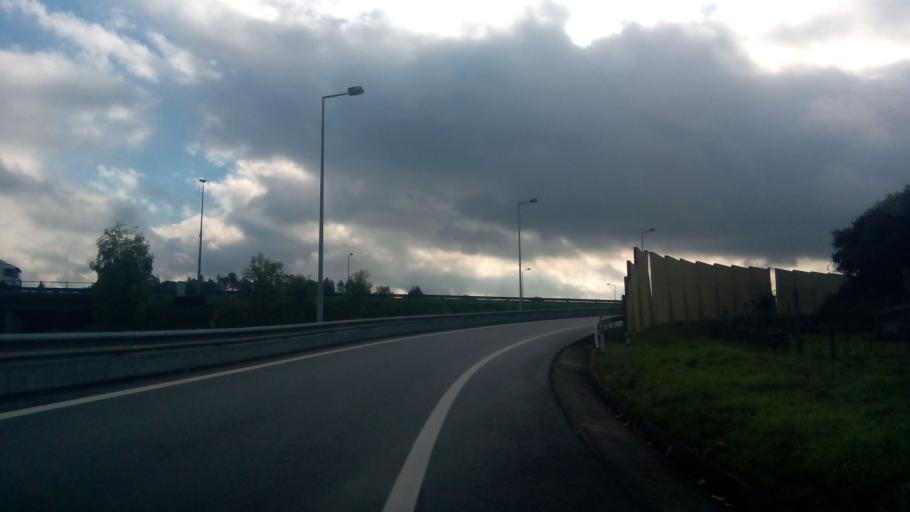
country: PT
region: Porto
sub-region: Paredes
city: Casteloes de Cepeda
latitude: 41.2001
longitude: -8.3383
